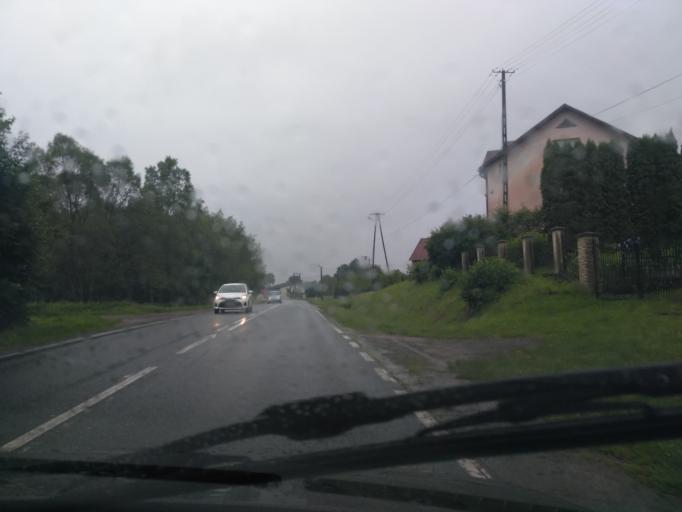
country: PL
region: Subcarpathian Voivodeship
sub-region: Powiat krosnienski
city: Leki
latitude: 49.8021
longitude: 21.6416
